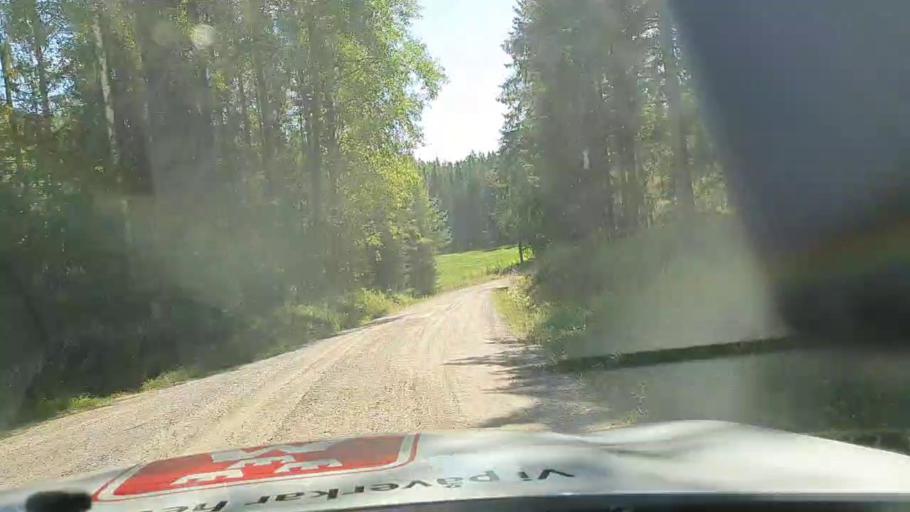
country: SE
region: Soedermanland
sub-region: Strangnas Kommun
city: Akers Styckebruk
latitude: 59.2015
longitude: 16.9188
